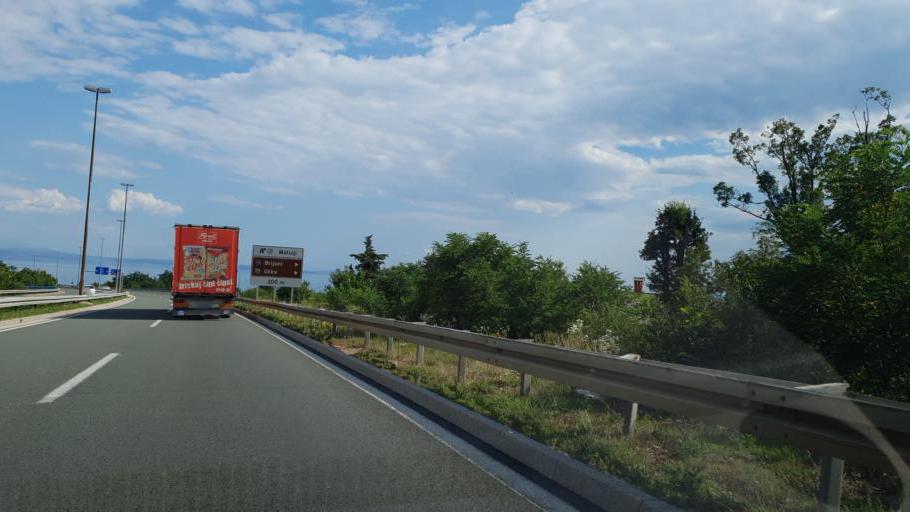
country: HR
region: Primorsko-Goranska
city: Matulji
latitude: 45.3690
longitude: 14.3268
